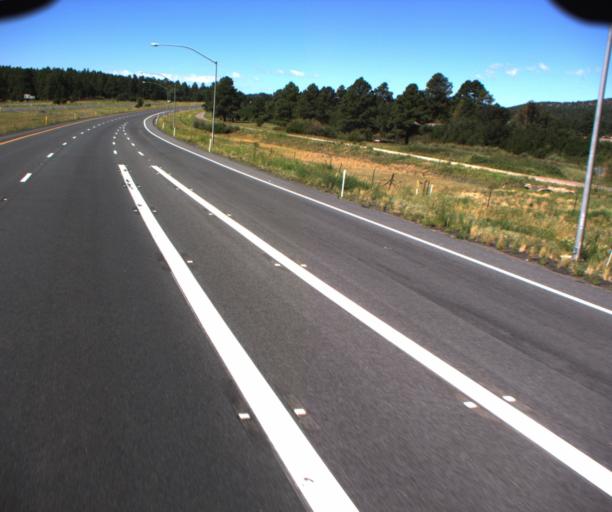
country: US
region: Arizona
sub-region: Coconino County
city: Williams
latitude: 35.2403
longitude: -112.2187
